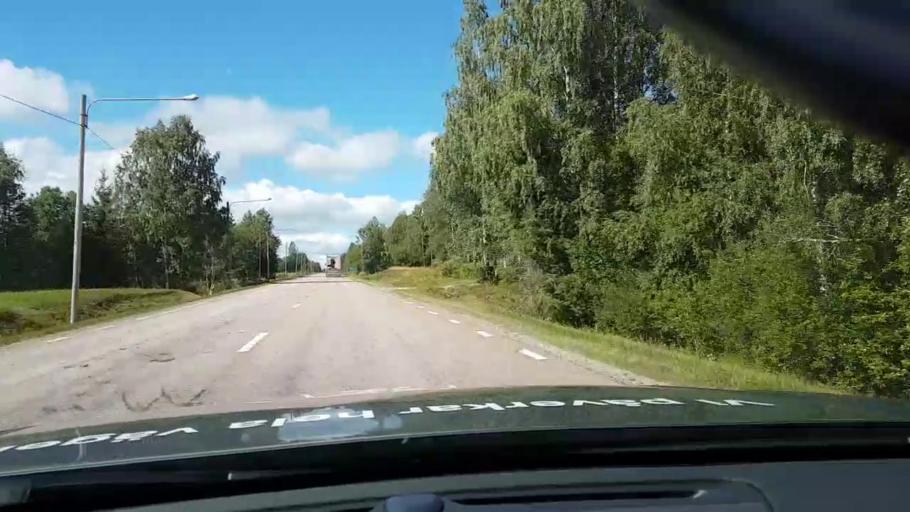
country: SE
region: Vaesternorrland
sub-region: OErnskoeldsviks Kommun
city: Bjasta
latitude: 63.3813
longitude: 18.4106
